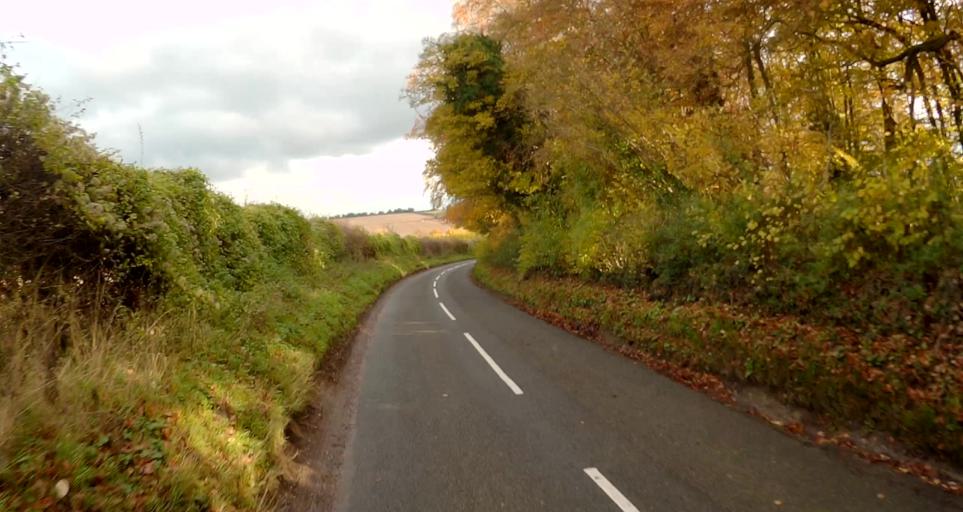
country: GB
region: England
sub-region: Hampshire
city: Old Basing
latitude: 51.2480
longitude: -1.0479
